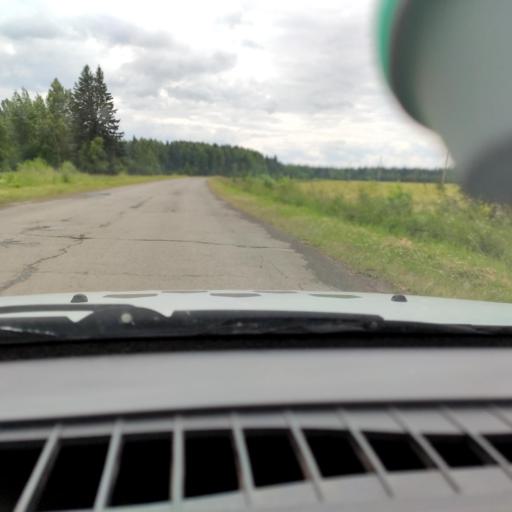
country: RU
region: Perm
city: Uinskoye
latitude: 57.1316
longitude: 56.5663
